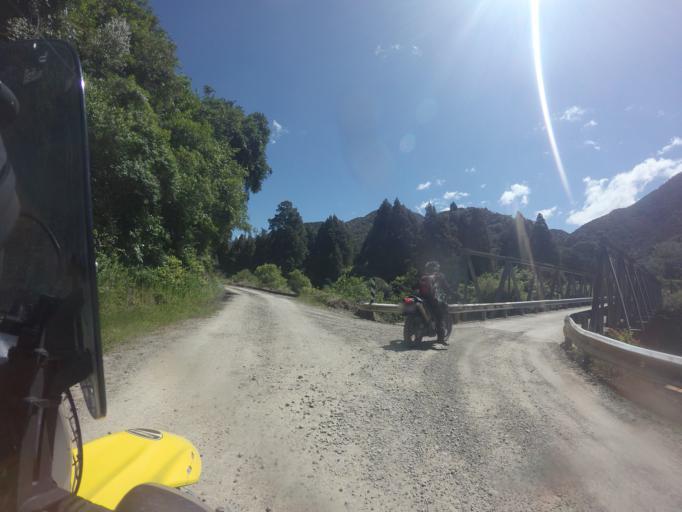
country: NZ
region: Bay of Plenty
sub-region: Opotiki District
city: Opotiki
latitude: -38.2945
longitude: 177.3388
